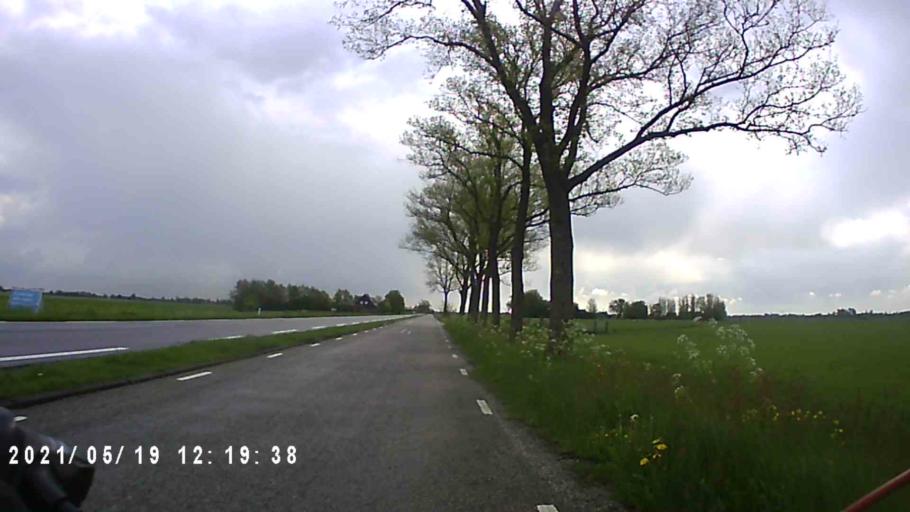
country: NL
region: Friesland
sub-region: Gemeente Kollumerland en Nieuwkruisland
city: Kollum
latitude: 53.2612
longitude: 6.1757
